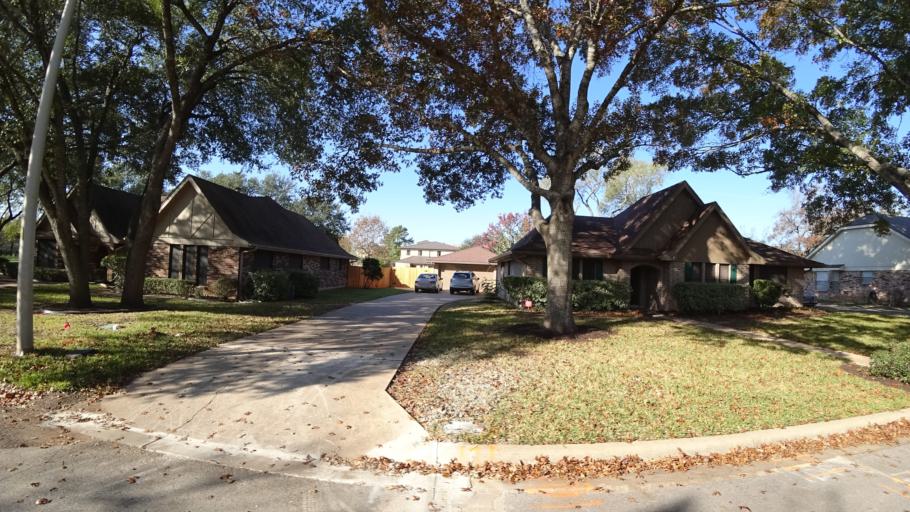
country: US
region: Texas
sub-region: Travis County
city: Shady Hollow
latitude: 30.2188
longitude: -97.8482
